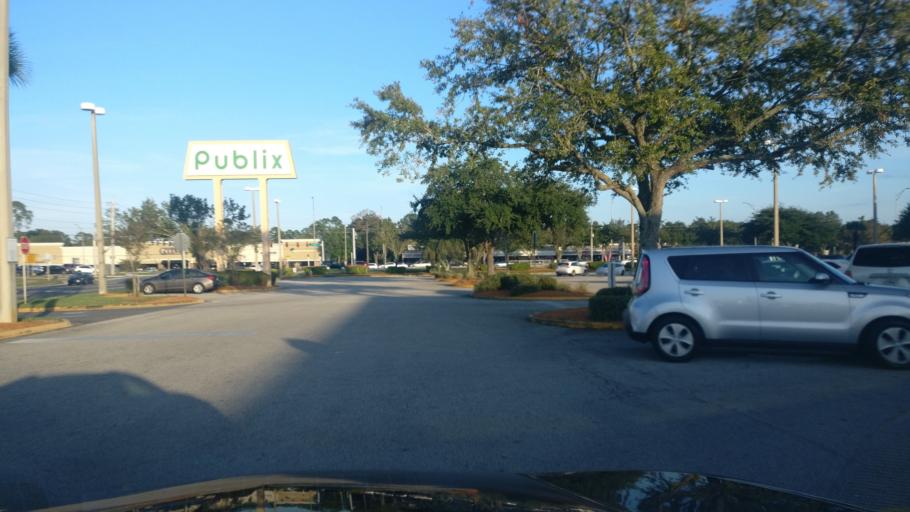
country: US
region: Florida
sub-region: Saint Johns County
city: Fruit Cove
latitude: 30.2205
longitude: -81.5535
